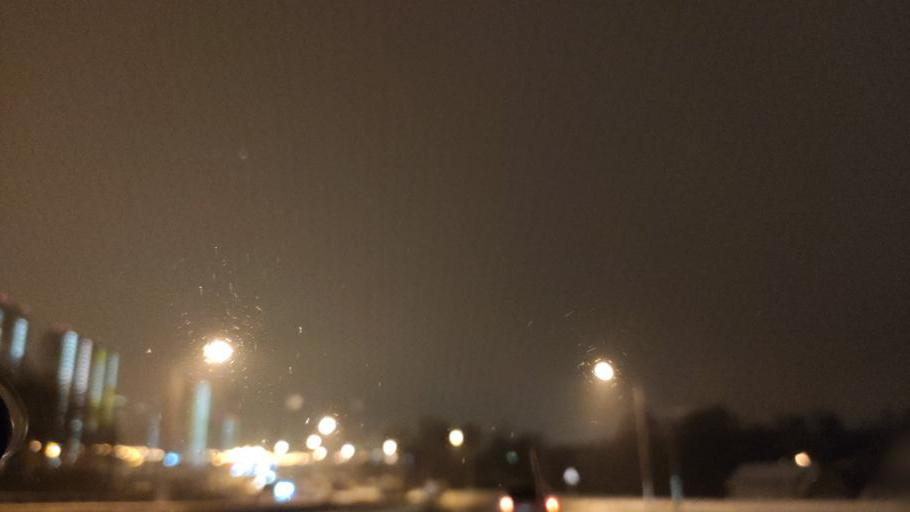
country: RU
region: Moskovskaya
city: Shcherbinka
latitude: 55.5250
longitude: 37.6050
